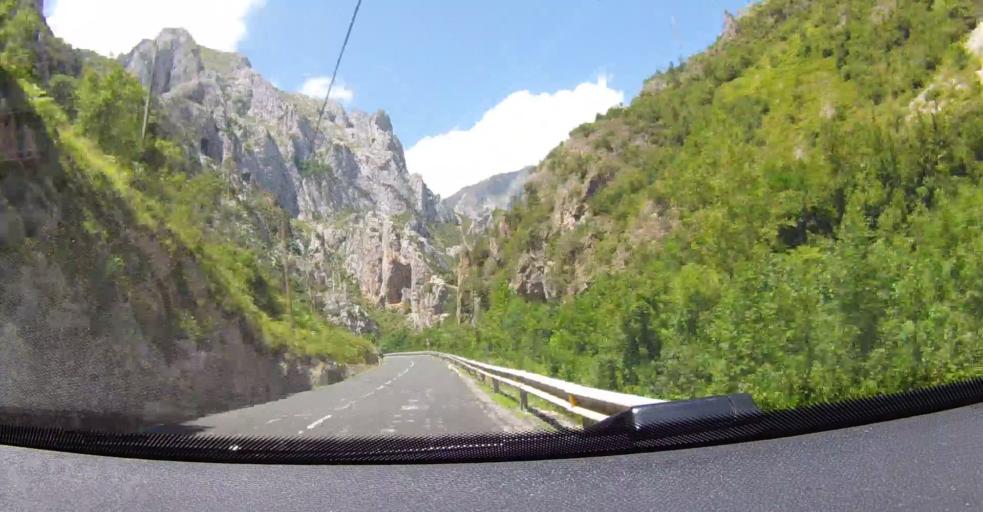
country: ES
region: Cantabria
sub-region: Provincia de Cantabria
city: Tresviso
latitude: 43.2655
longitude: -4.6289
